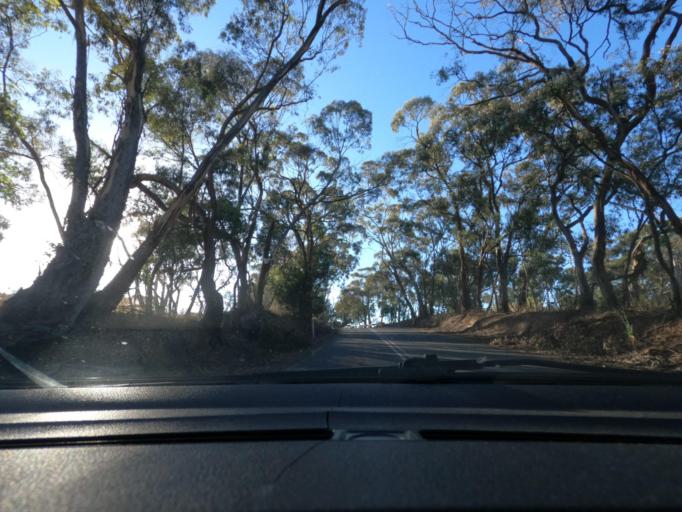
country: AU
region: South Australia
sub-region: Clare and Gilbert Valleys
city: Clare
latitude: -33.9043
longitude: 138.6573
